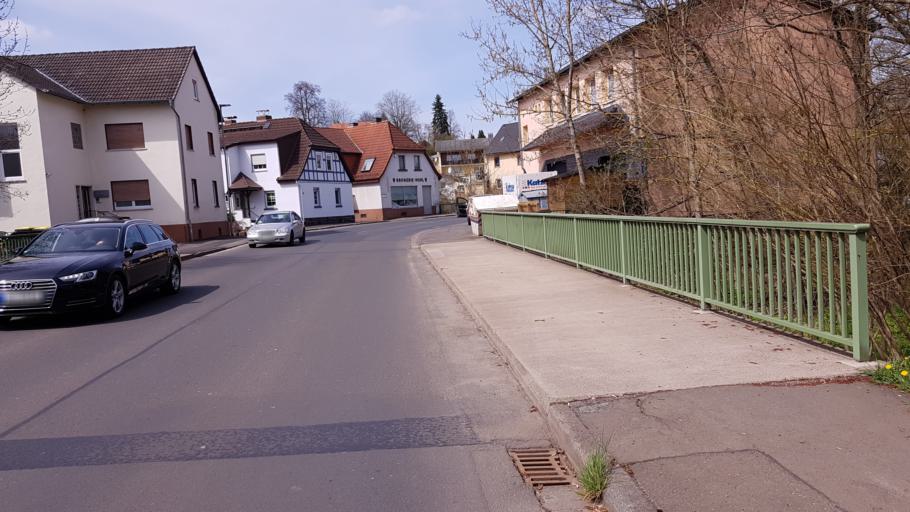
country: DE
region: Hesse
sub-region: Regierungsbezirk Giessen
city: Grunberg
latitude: 50.6472
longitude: 9.0286
